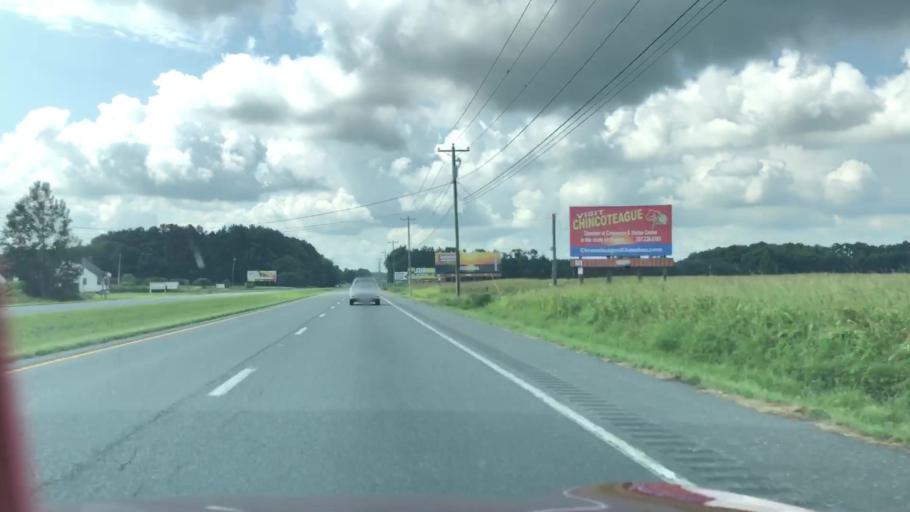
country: US
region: Virginia
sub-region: Accomack County
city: Wattsville
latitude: 37.9682
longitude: -75.5326
